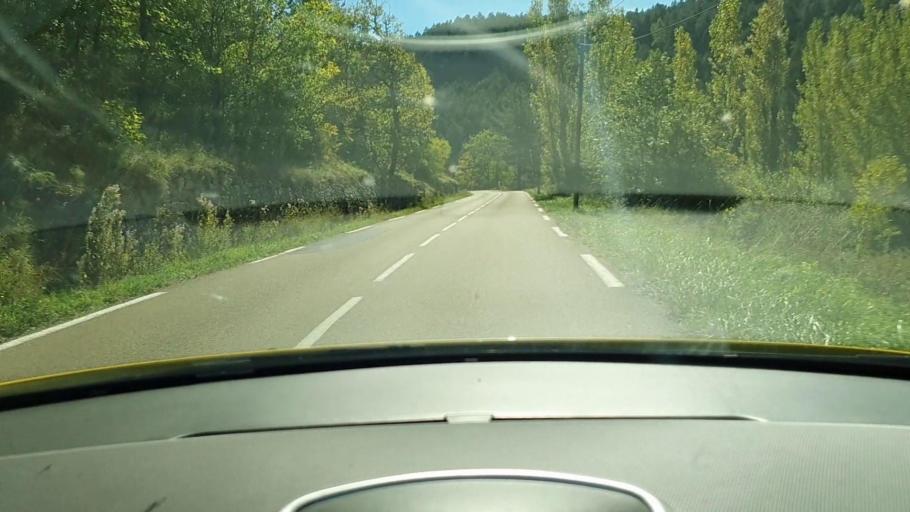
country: FR
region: Languedoc-Roussillon
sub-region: Departement du Gard
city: Le Vigan
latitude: 43.9667
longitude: 3.4305
